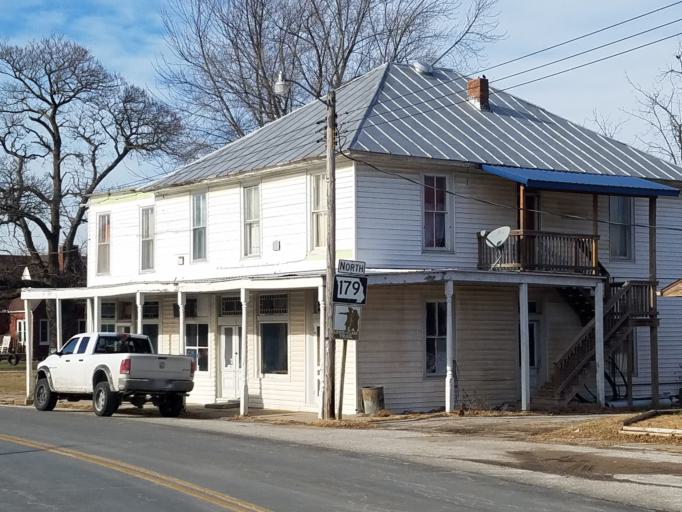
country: US
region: Missouri
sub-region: Moniteau County
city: California
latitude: 38.7655
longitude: -92.4808
